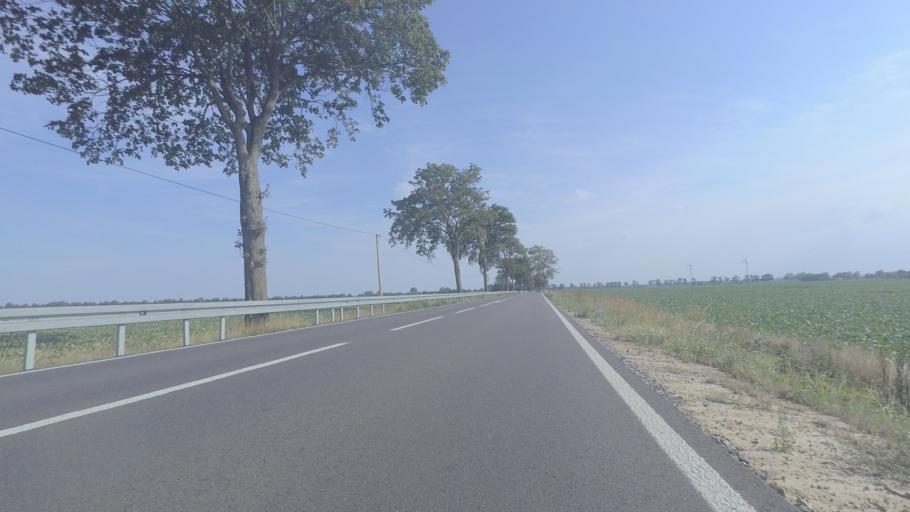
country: DE
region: Mecklenburg-Vorpommern
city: Gormin
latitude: 54.0081
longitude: 13.1422
